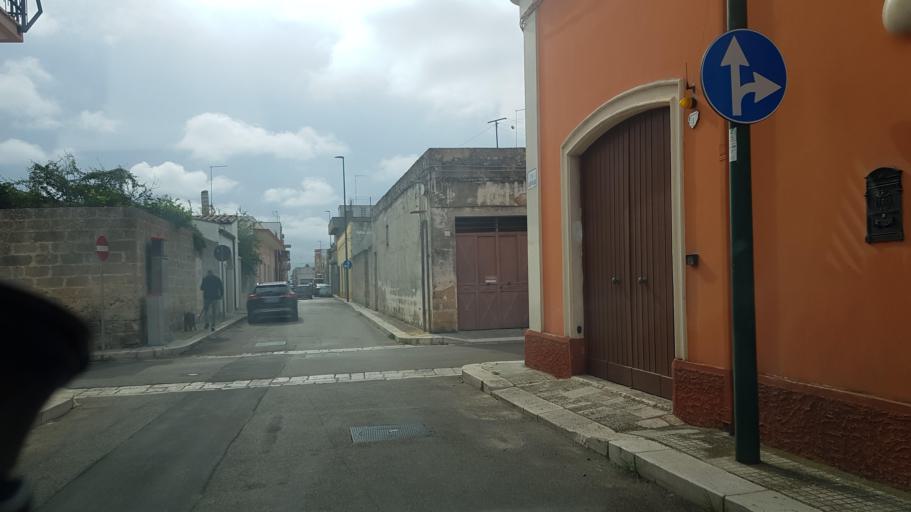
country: IT
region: Apulia
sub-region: Provincia di Lecce
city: Guagnano
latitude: 40.4027
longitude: 17.9480
